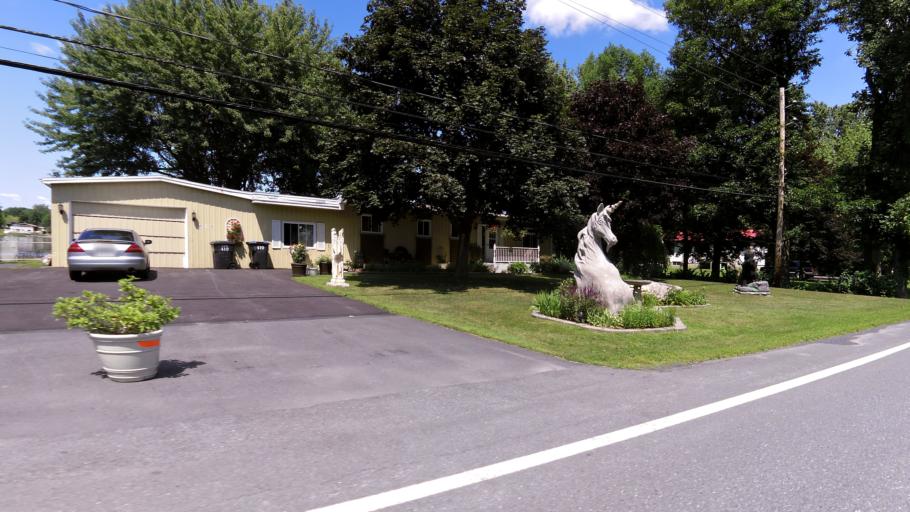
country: CA
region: Quebec
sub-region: Monteregie
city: Saint-Jean-sur-Richelieu
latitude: 45.3524
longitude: -73.2520
